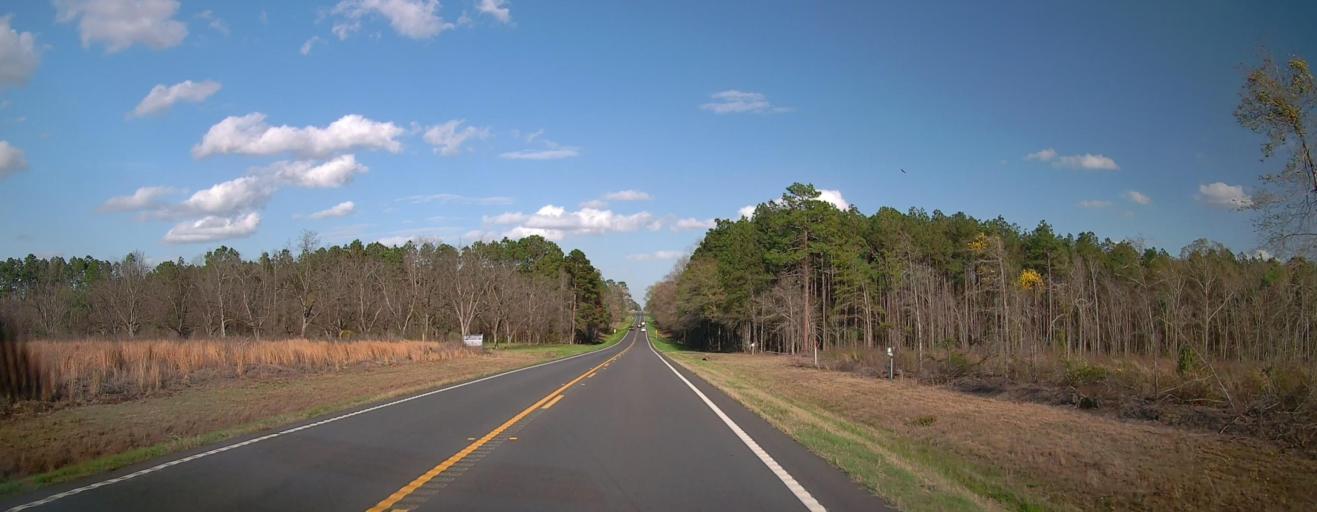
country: US
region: Georgia
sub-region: Montgomery County
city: Mount Vernon
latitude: 32.1840
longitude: -82.5401
